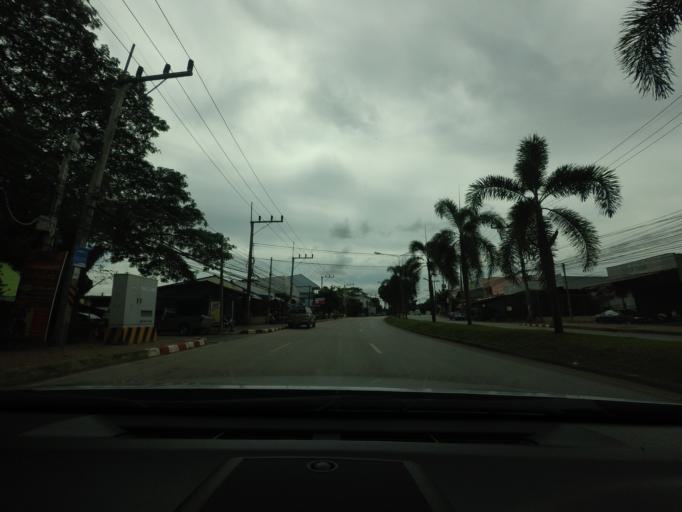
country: TH
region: Songkhla
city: Sadao
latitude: 6.6630
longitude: 100.3299
